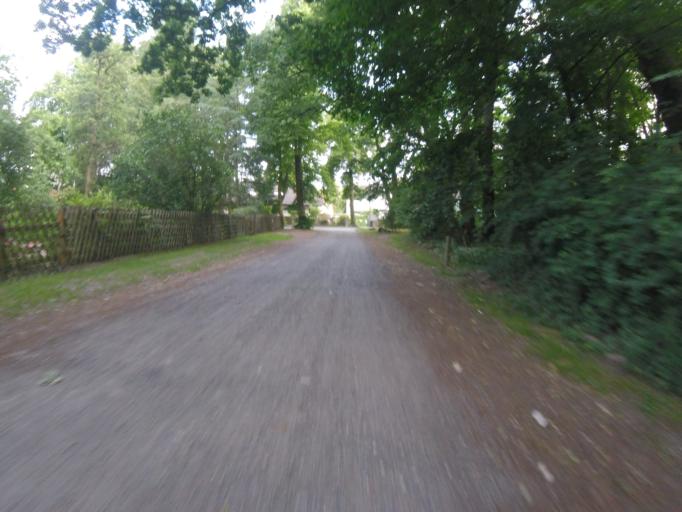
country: DE
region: Brandenburg
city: Konigs Wusterhausen
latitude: 52.2792
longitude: 13.6341
